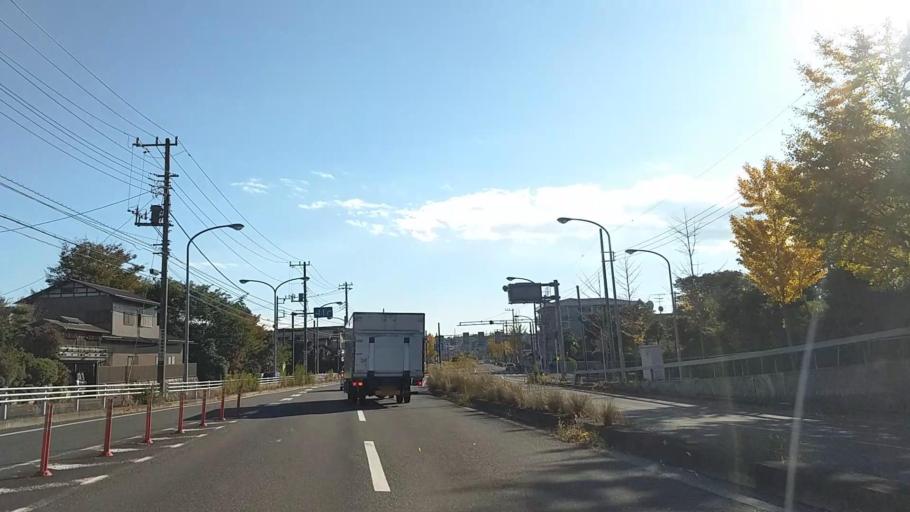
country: JP
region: Kanagawa
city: Yokohama
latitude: 35.5233
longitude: 139.5687
